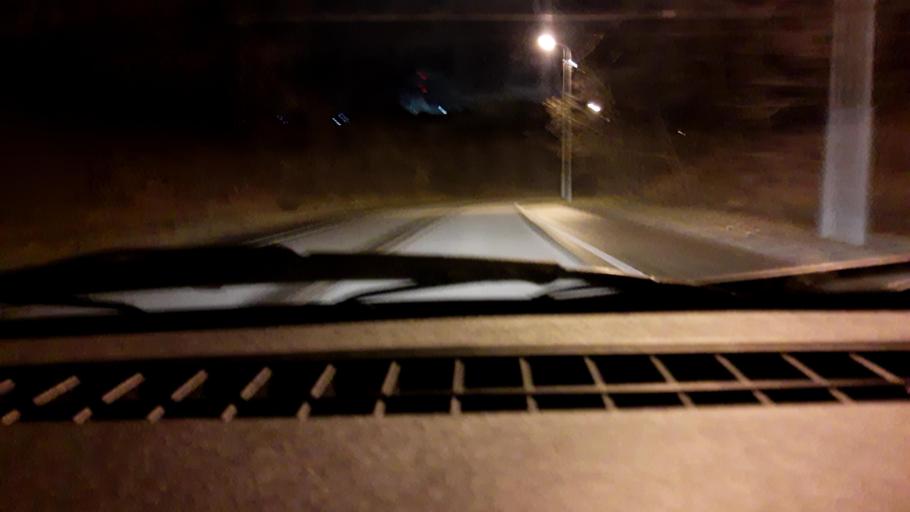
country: RU
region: Bashkortostan
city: Ufa
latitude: 54.8829
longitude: 56.0566
